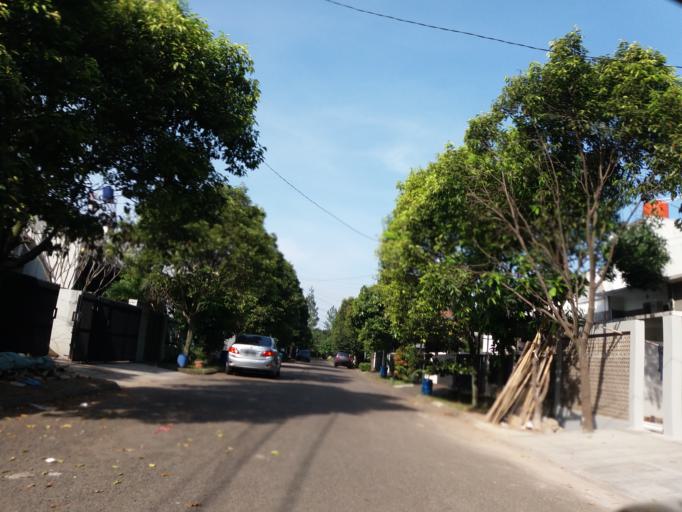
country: ID
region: West Java
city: Bandung
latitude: -6.9621
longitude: 107.6328
